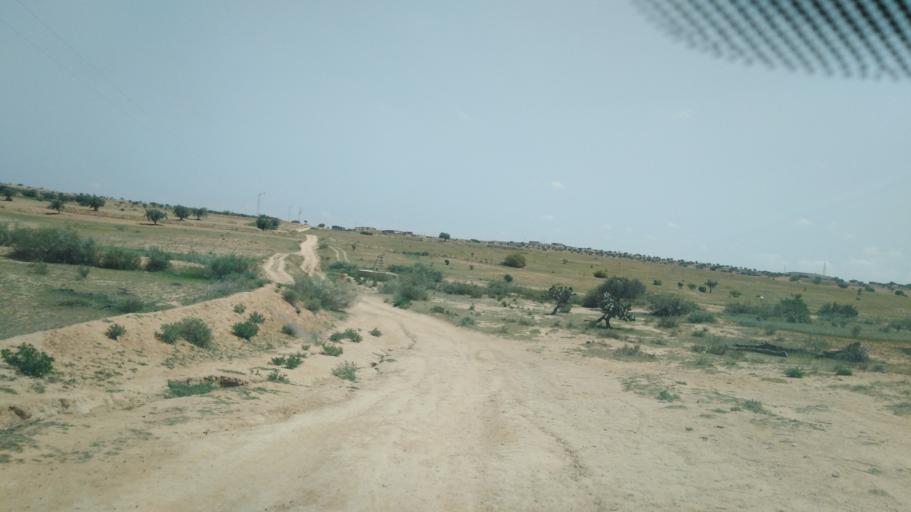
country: TN
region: Safaqis
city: Sfax
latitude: 34.7667
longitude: 10.5662
